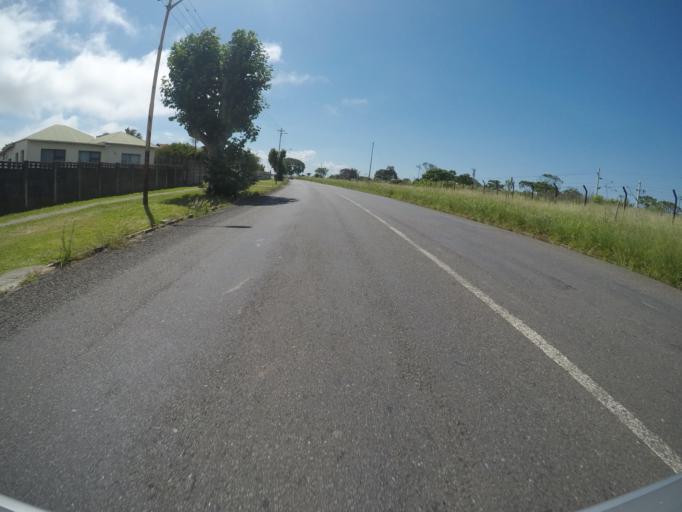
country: ZA
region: Eastern Cape
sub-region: Buffalo City Metropolitan Municipality
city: East London
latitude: -32.9760
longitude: 27.8978
